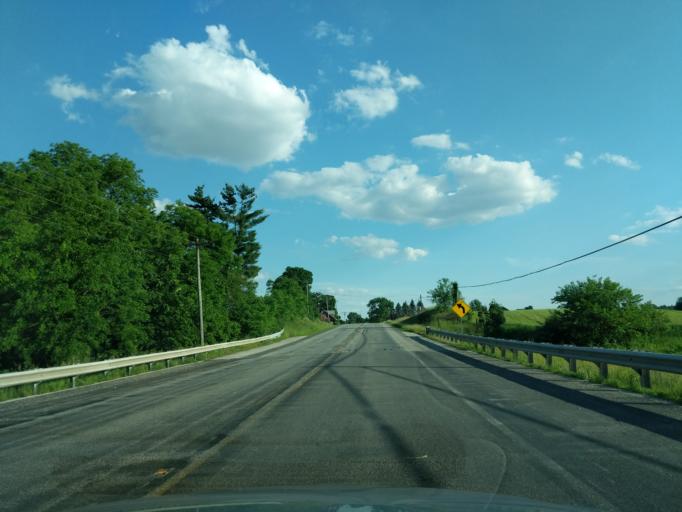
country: US
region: Indiana
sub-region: Whitley County
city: Columbia City
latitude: 41.1260
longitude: -85.4813
